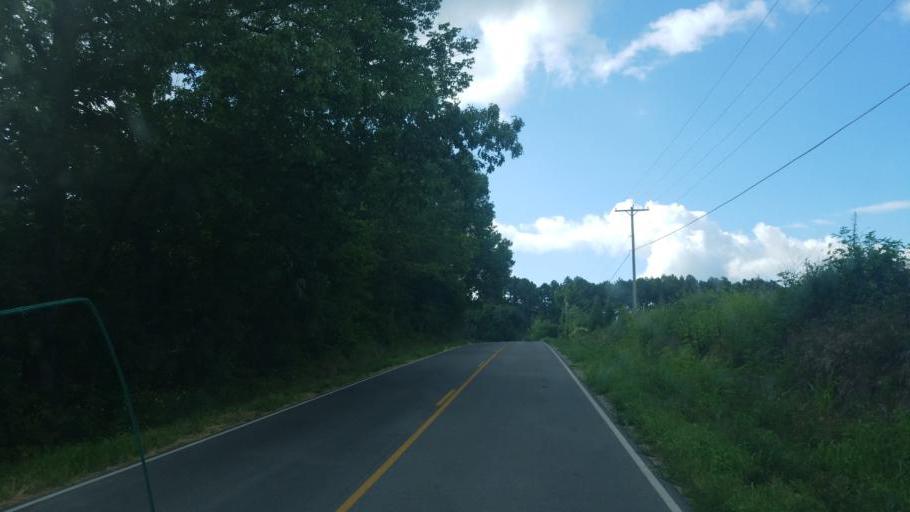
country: US
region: Illinois
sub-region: Union County
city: Cobden
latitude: 37.5668
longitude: -89.3115
